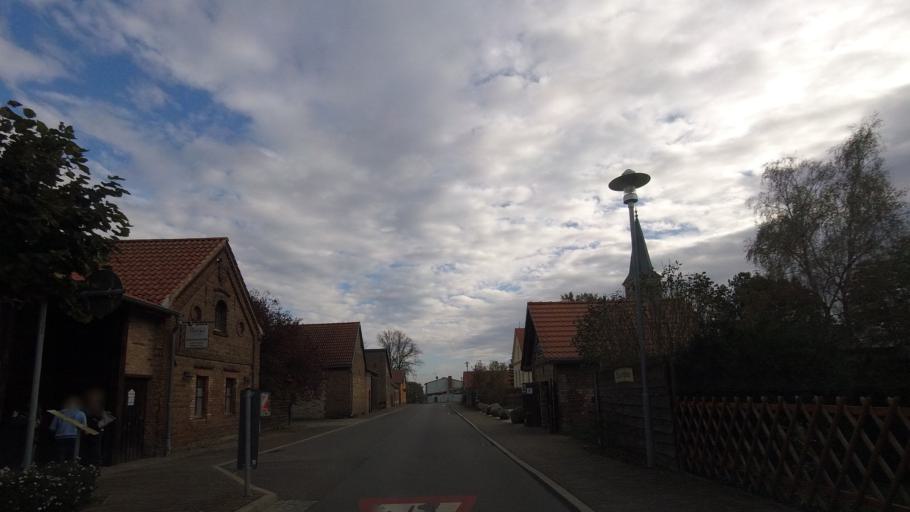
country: DE
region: Brandenburg
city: Borkheide
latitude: 52.2106
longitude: 12.8991
